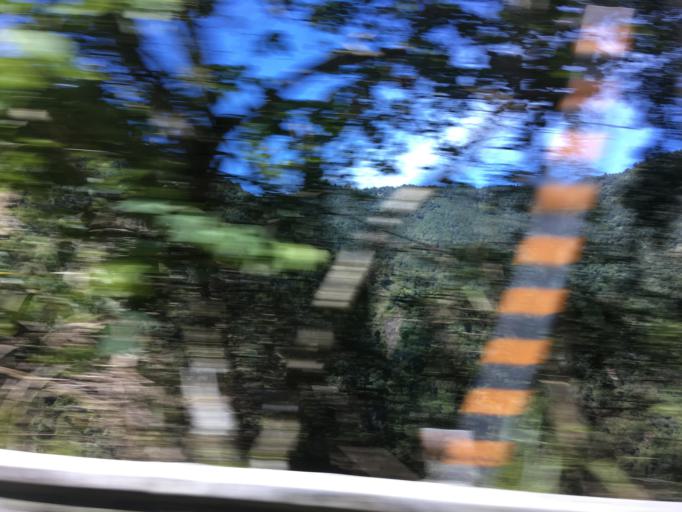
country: TW
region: Taiwan
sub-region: Yilan
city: Yilan
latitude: 24.5560
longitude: 121.5022
